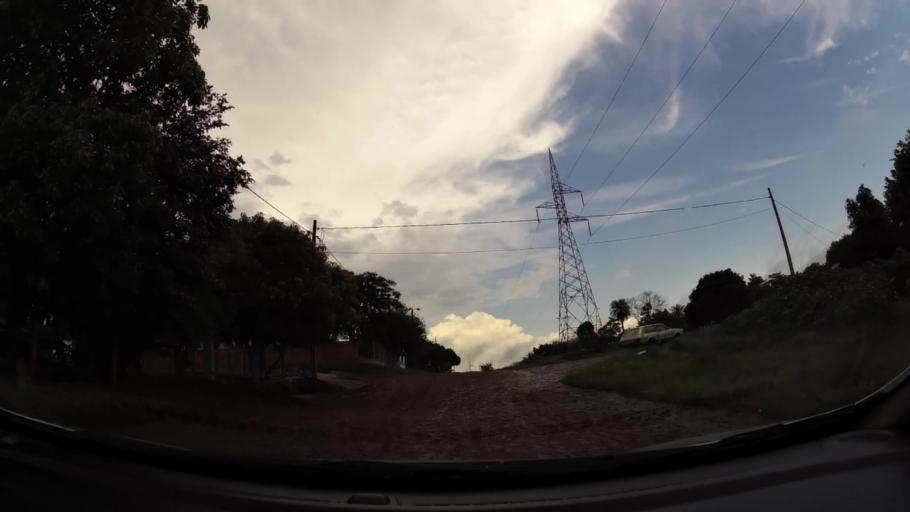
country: PY
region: Alto Parana
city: Presidente Franco
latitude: -25.5344
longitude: -54.6655
